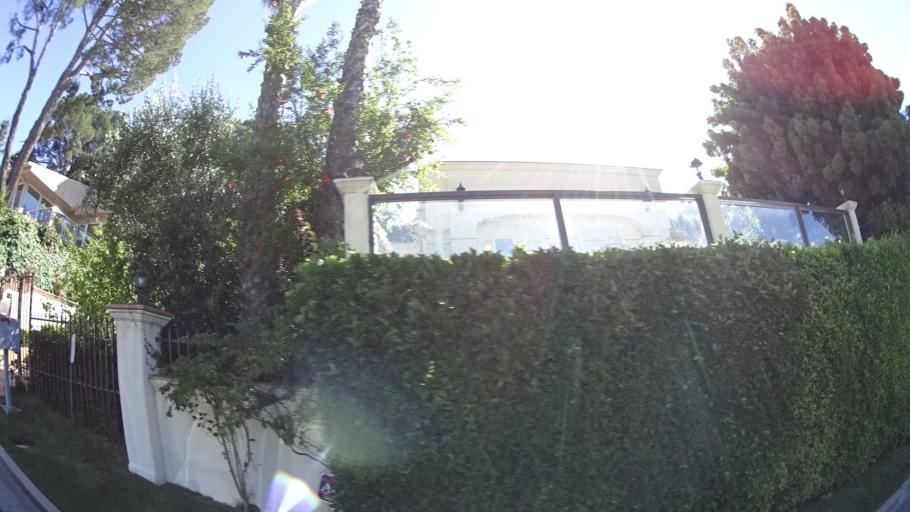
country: US
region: California
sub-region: Los Angeles County
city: Sherman Oaks
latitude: 34.1315
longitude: -118.4616
